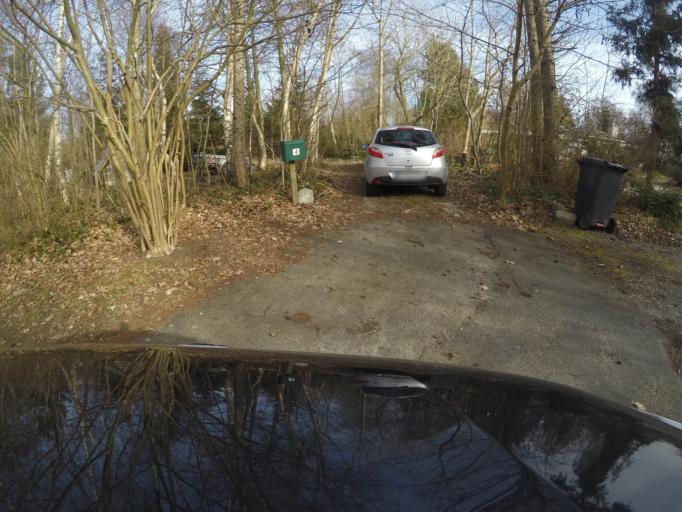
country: DK
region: Capital Region
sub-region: Halsnaes Kommune
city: Liseleje
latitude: 55.9931
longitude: 11.9277
